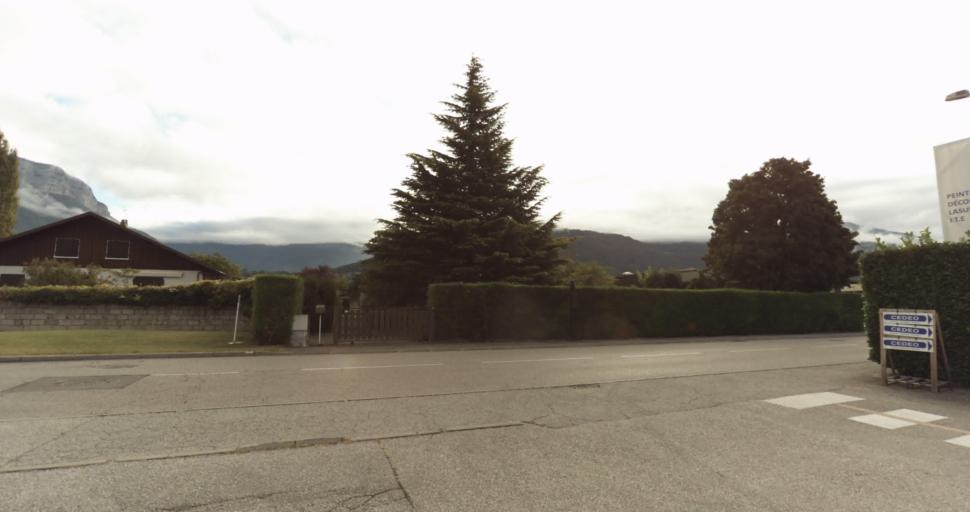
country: FR
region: Rhone-Alpes
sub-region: Departement de la Savoie
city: La Ravoire
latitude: 45.5699
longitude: 5.9637
